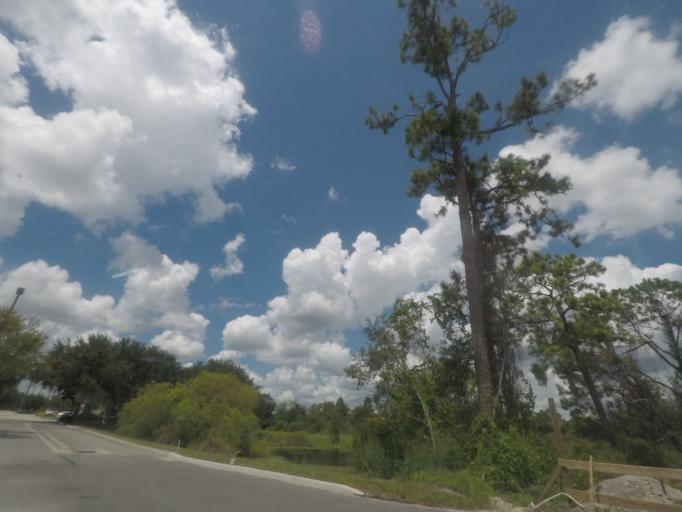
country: US
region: Florida
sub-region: Polk County
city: Citrus Ridge
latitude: 28.3480
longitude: -81.6113
